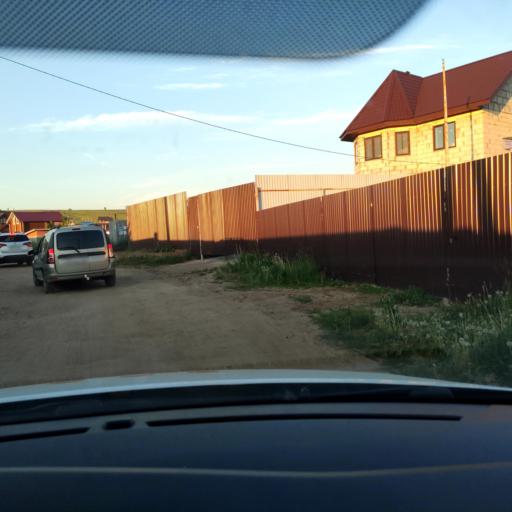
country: RU
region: Tatarstan
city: Stolbishchi
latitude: 55.7466
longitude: 49.3088
